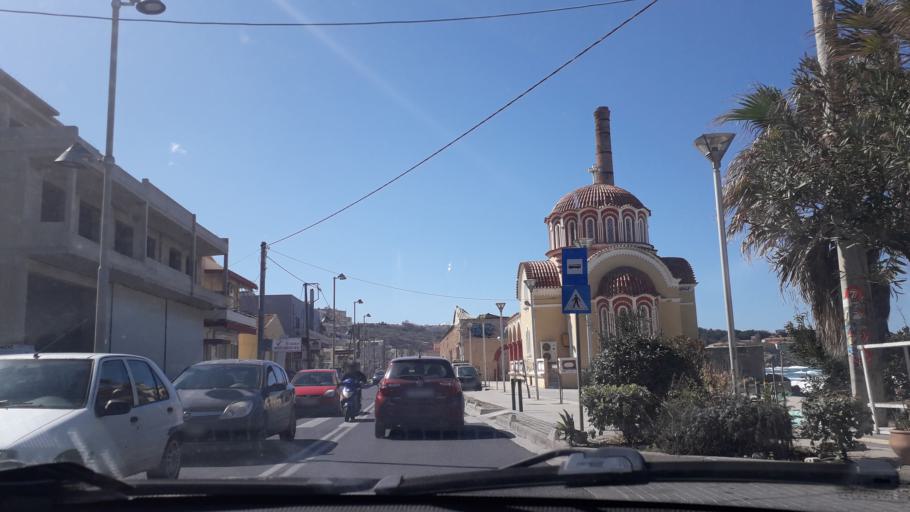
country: GR
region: Crete
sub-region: Nomos Rethymnis
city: Rethymno
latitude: 35.3646
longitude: 24.4618
